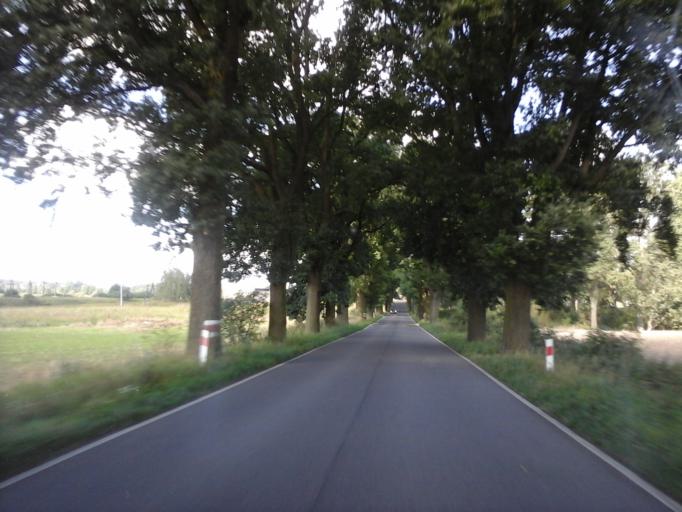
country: PL
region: West Pomeranian Voivodeship
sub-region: Powiat stargardzki
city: Dolice
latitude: 53.1964
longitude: 15.2261
